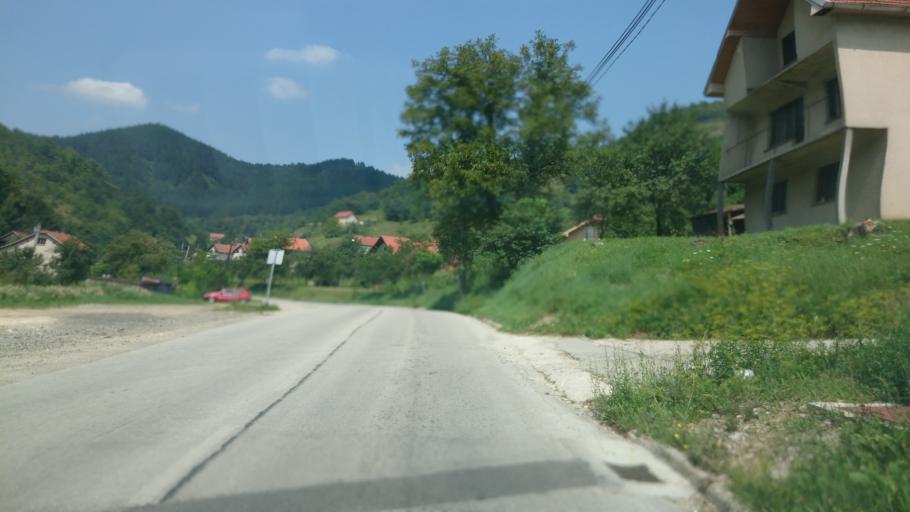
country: BA
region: Federation of Bosnia and Herzegovina
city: Lokvine
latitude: 44.1892
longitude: 17.8594
